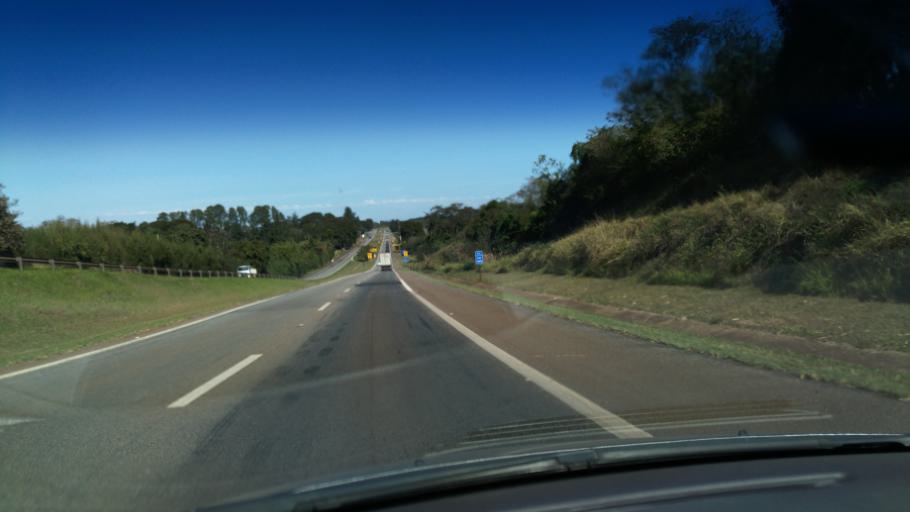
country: BR
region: Sao Paulo
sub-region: Santo Antonio De Posse
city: Santo Antonio de Posse
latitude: -22.5550
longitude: -46.9991
